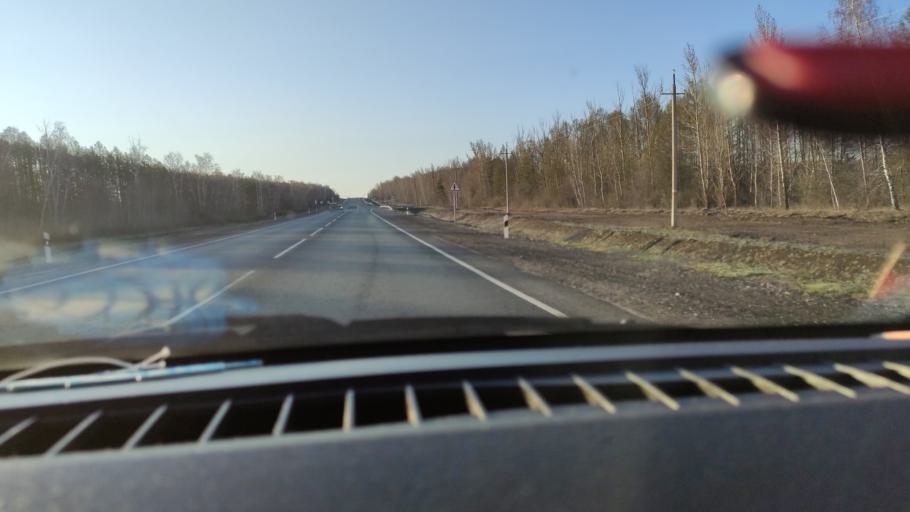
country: RU
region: Saratov
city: Shikhany
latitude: 52.1504
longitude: 47.1889
